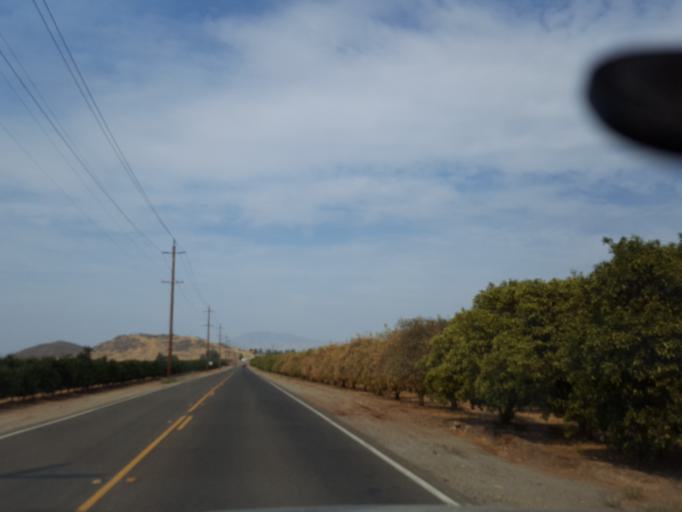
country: US
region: California
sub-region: Tulare County
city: Orosi
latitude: 36.5880
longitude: -119.2871
